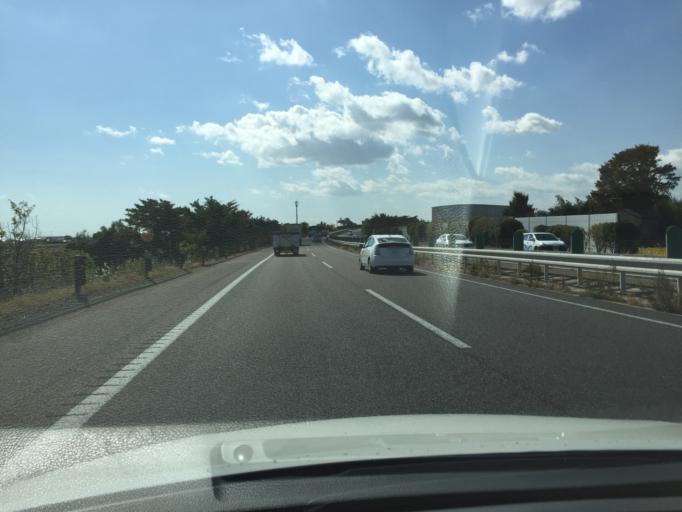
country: JP
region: Fukushima
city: Koriyama
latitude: 37.4429
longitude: 140.3512
